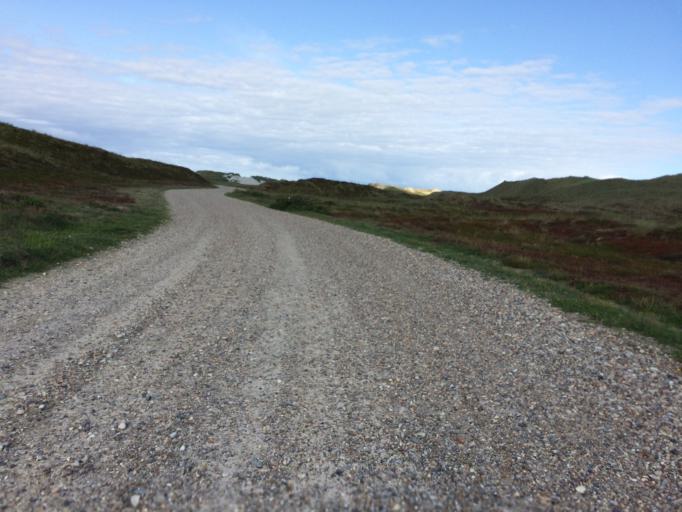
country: DK
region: Central Jutland
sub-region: Ringkobing-Skjern Kommune
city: Hvide Sande
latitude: 55.8961
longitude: 8.1642
